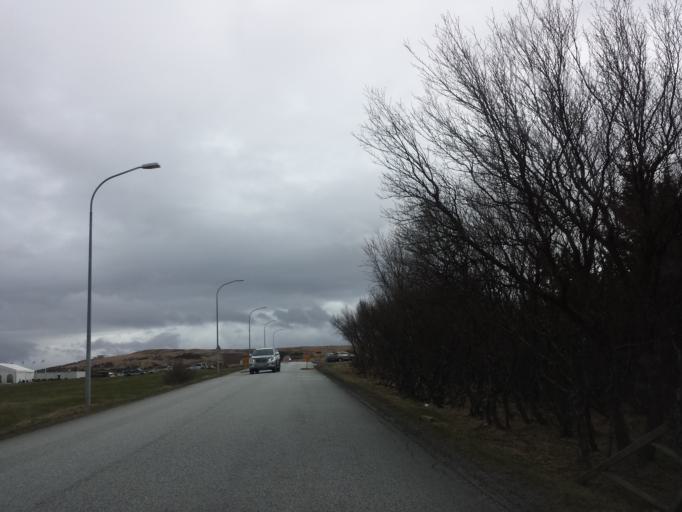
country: IS
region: Capital Region
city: Gardabaer
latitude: 64.0832
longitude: -21.8863
